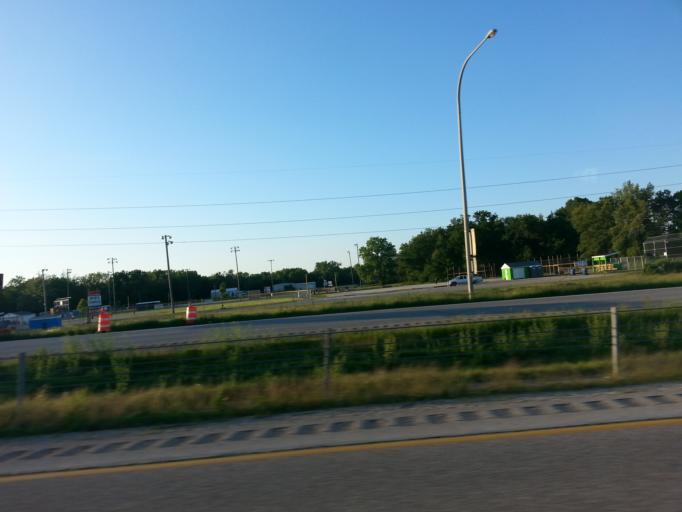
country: US
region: Illinois
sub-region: Vermilion County
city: Tilton
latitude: 40.1048
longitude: -87.6440
